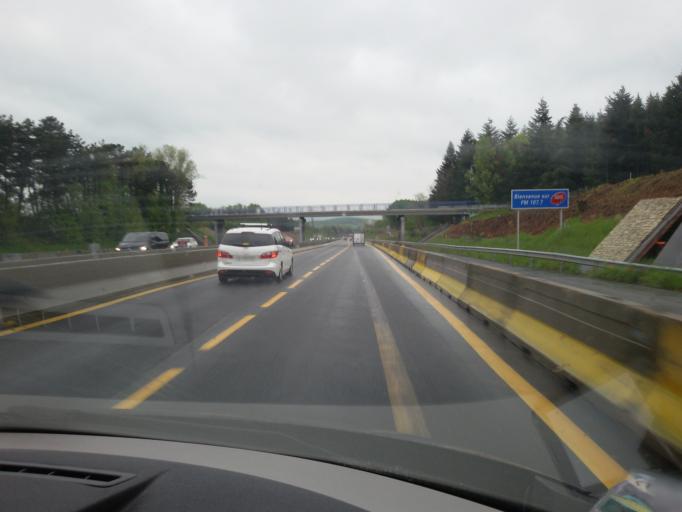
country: FR
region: Rhone-Alpes
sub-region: Departement du Rhone
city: Limonest
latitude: 45.8388
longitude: 4.7549
